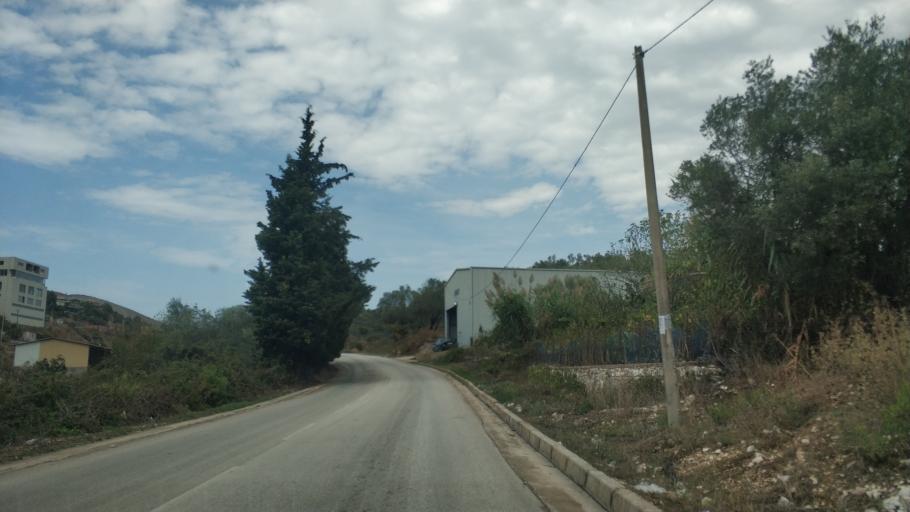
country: AL
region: Vlore
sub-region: Rrethi i Sarandes
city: Sarande
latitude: 39.8721
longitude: 20.0308
